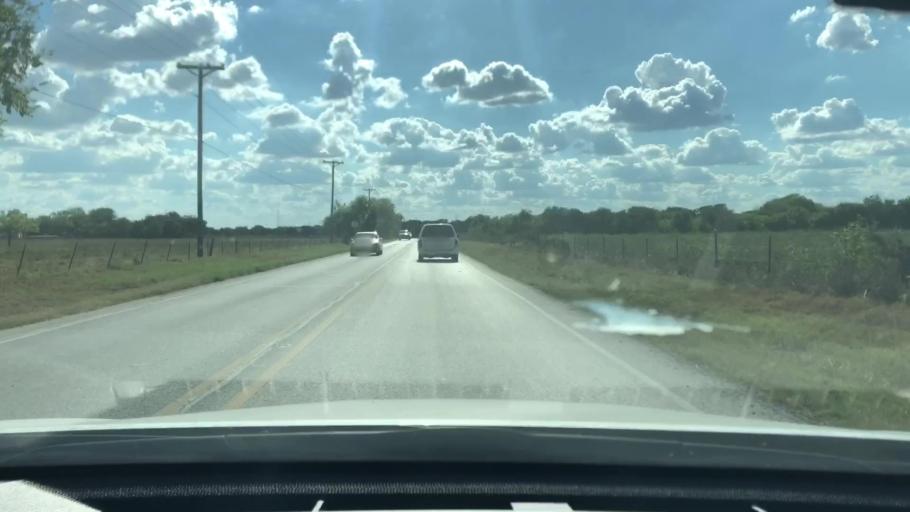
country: US
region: Texas
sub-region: Guadalupe County
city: Northcliff
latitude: 29.6569
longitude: -98.2044
